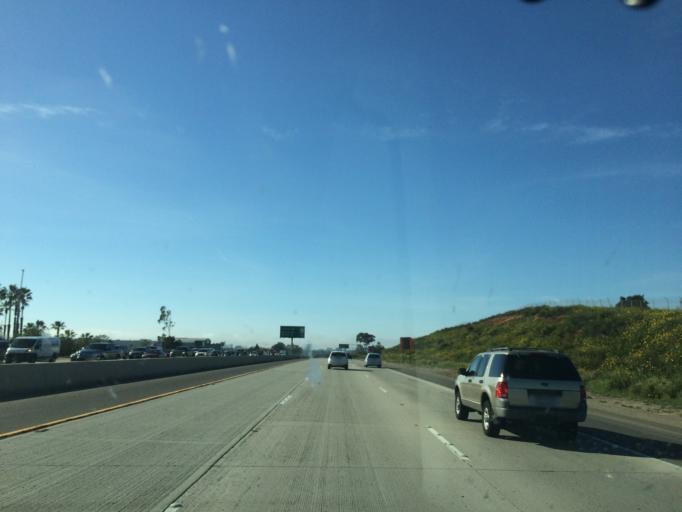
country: US
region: California
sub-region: San Diego County
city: La Jolla
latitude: 32.8393
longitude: -117.1610
